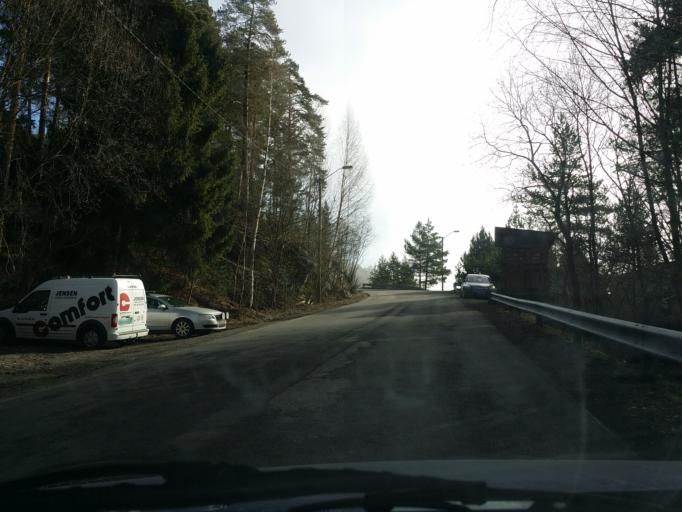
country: NO
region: Buskerud
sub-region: Nedre Eiker
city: Mjondalen
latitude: 59.7622
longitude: 10.0346
